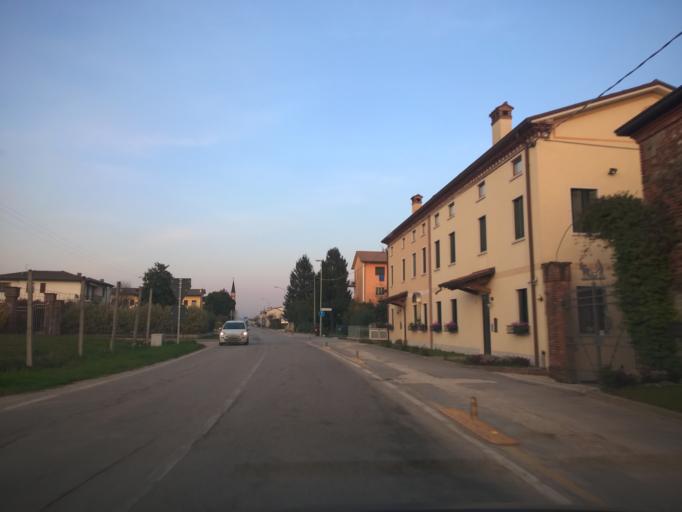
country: IT
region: Veneto
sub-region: Provincia di Vicenza
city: Villaverla
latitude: 45.6696
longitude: 11.4596
